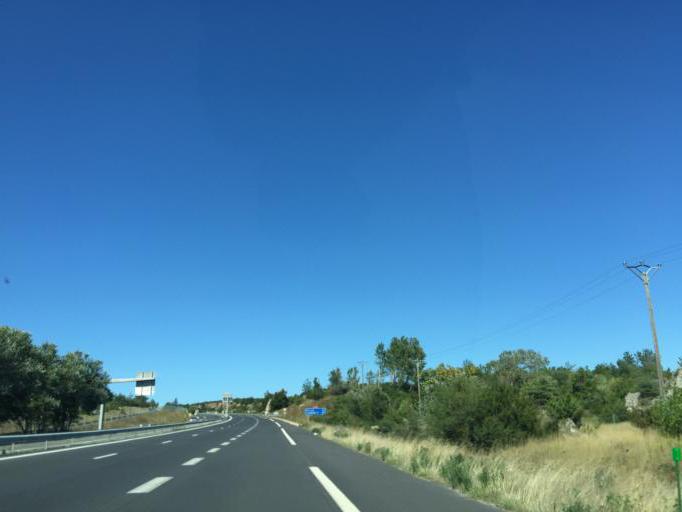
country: FR
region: Languedoc-Roussillon
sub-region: Departement de l'Herault
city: Lodeve
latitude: 43.8688
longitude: 3.3115
